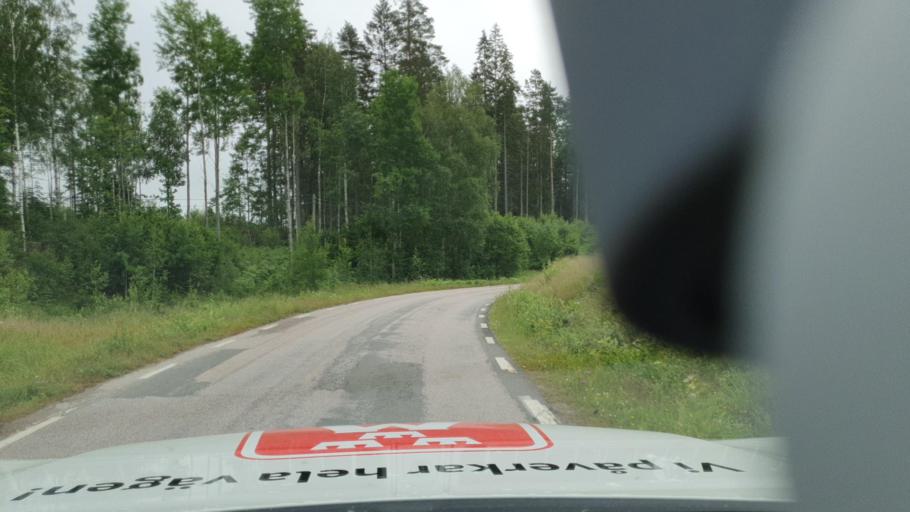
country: SE
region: Vaestra Goetaland
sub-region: Gullspangs Kommun
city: Gullspang
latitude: 59.0381
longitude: 14.1558
